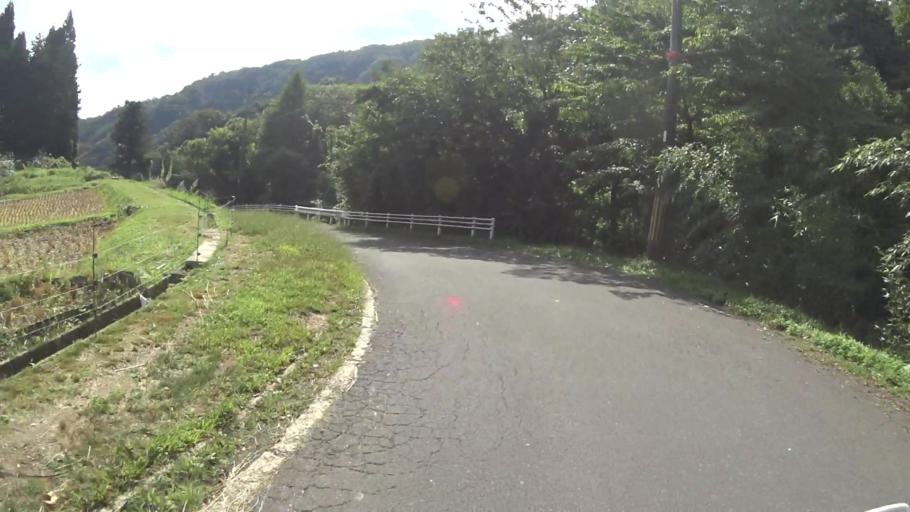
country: JP
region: Kyoto
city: Miyazu
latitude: 35.6356
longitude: 135.1911
